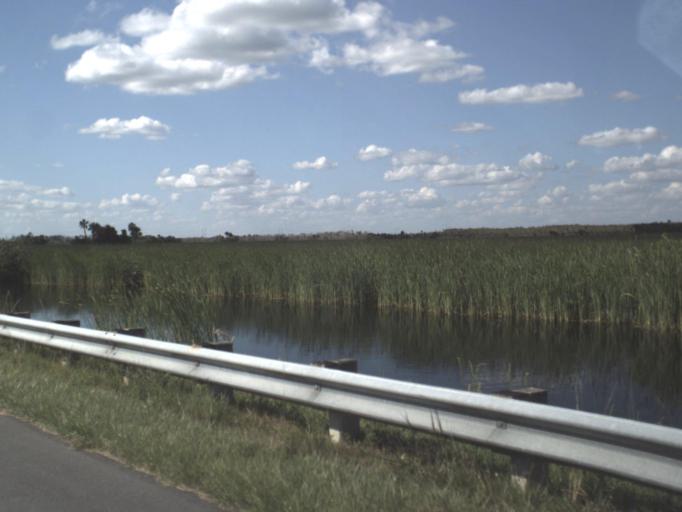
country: US
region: Florida
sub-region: Collier County
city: Marco
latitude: 25.9062
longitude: -81.3510
